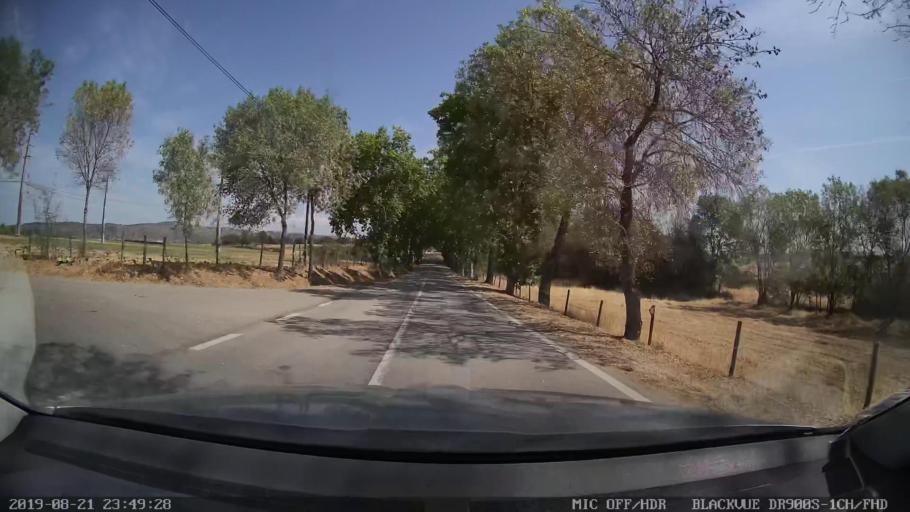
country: PT
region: Castelo Branco
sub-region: Idanha-A-Nova
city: Idanha-a-Nova
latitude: 39.8781
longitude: -7.2502
